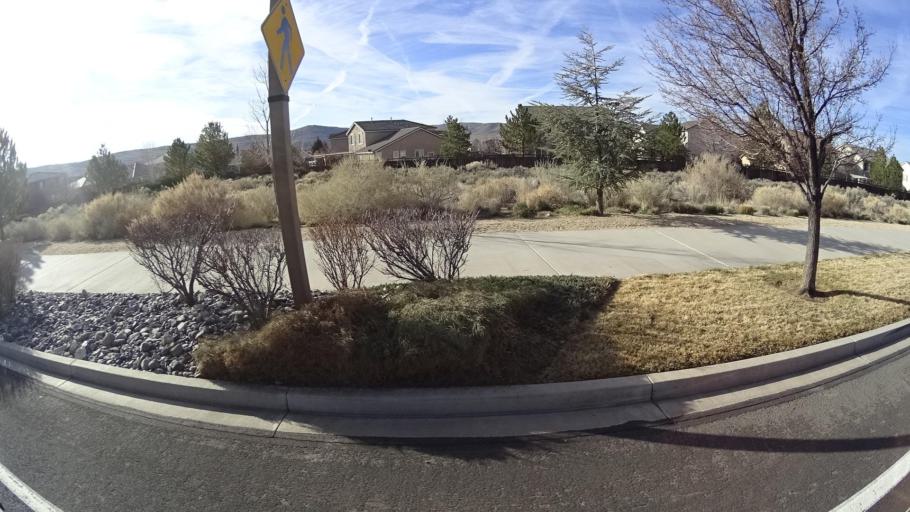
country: US
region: Nevada
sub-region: Washoe County
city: Spanish Springs
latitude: 39.6232
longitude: -119.6737
